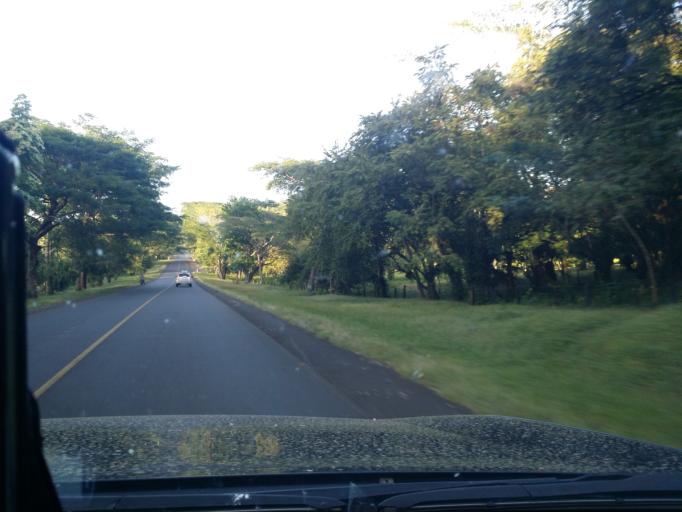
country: NI
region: Rio San Juan
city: San Miguelito
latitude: 11.4758
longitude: -84.8468
